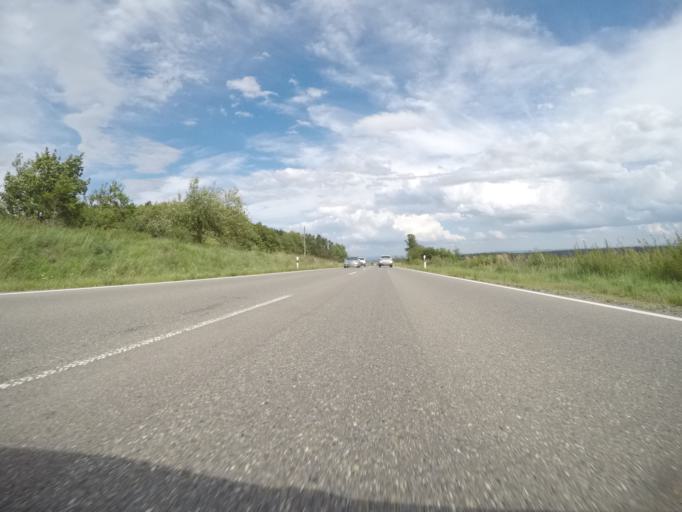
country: DE
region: Baden-Wuerttemberg
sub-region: Karlsruhe Region
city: Schopfloch
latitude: 48.4502
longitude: 8.5873
